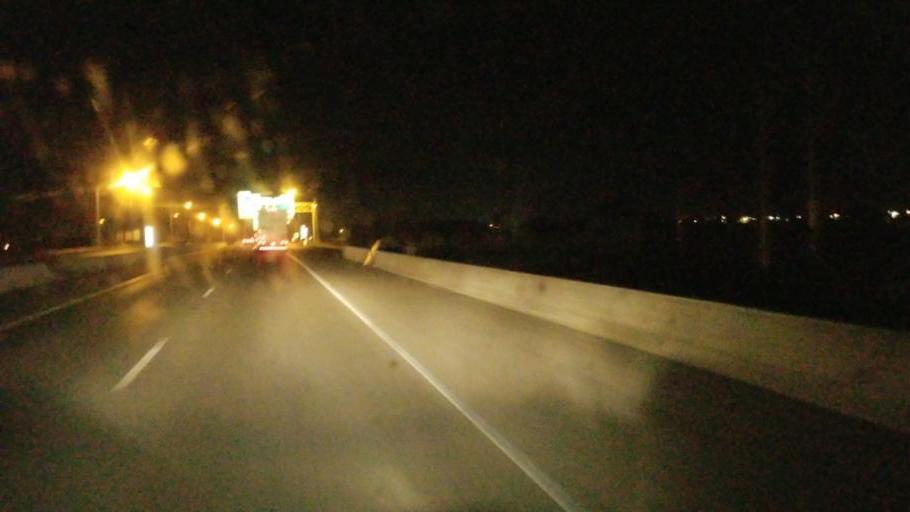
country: US
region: Indiana
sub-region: Allen County
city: Fort Wayne
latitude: 41.1683
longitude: -85.0951
